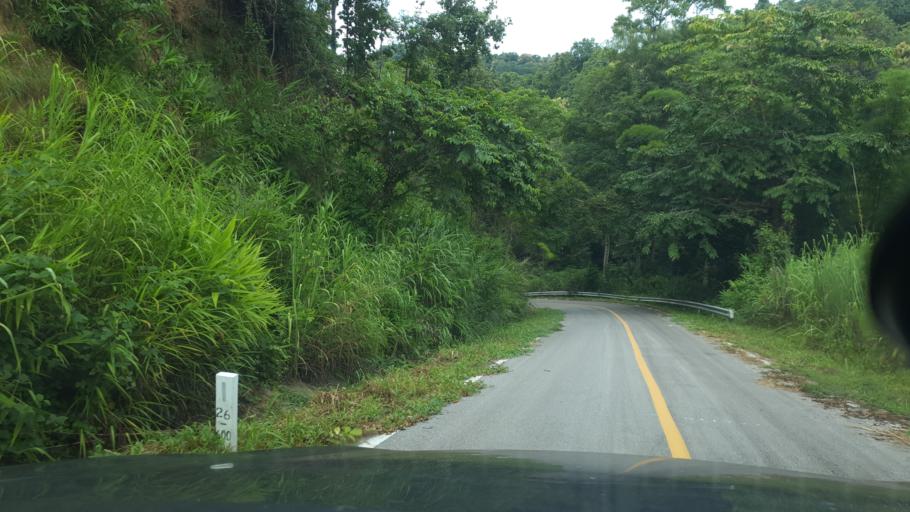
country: TH
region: Lamphun
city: Mae Tha
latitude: 18.4868
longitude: 99.2678
